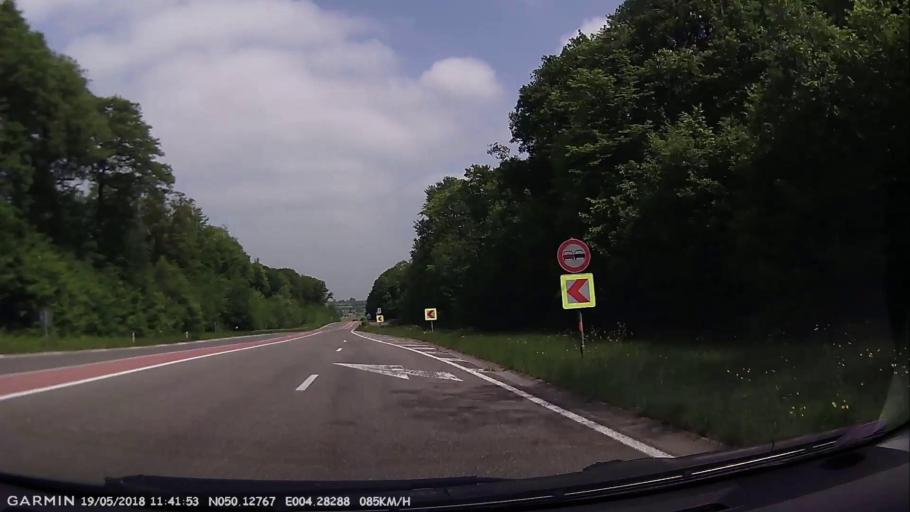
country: BE
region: Wallonia
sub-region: Province du Hainaut
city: Froidchapelle
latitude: 50.1279
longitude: 4.2831
